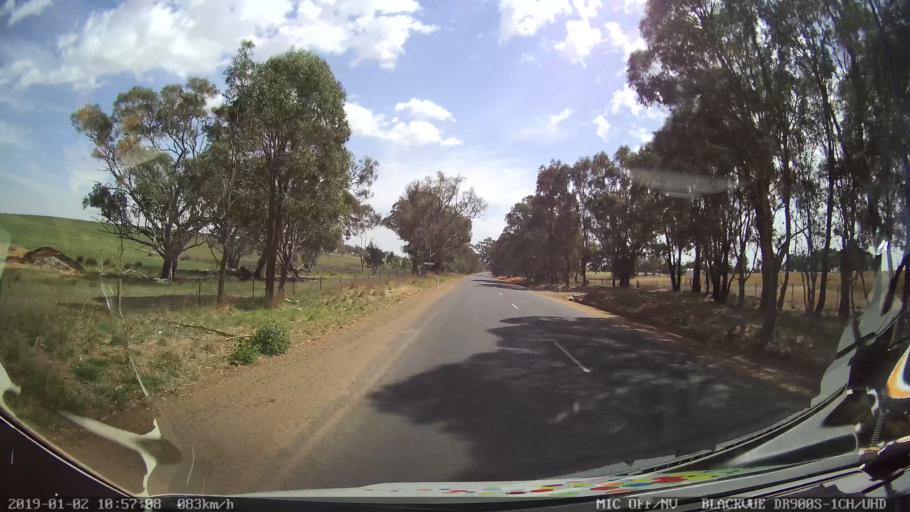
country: AU
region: New South Wales
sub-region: Cootamundra
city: Cootamundra
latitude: -34.6389
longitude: 148.2809
